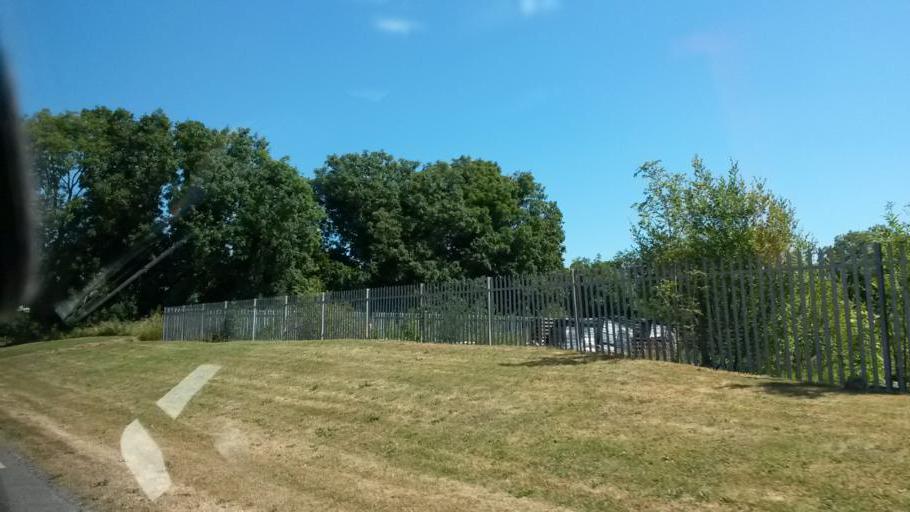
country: IE
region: Leinster
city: Ballymun
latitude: 53.4482
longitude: -6.2807
